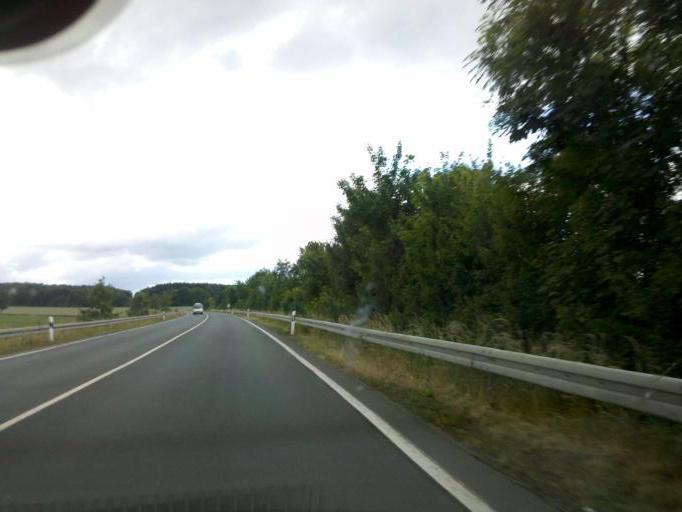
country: DE
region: North Rhine-Westphalia
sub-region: Regierungsbezirk Arnsberg
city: Anrochte
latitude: 51.5439
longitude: 8.3103
